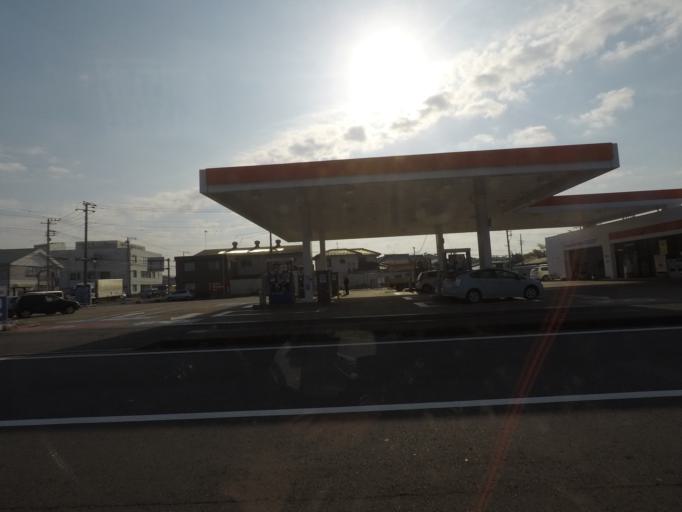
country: JP
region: Chiba
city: Narita
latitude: 35.7377
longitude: 140.3159
